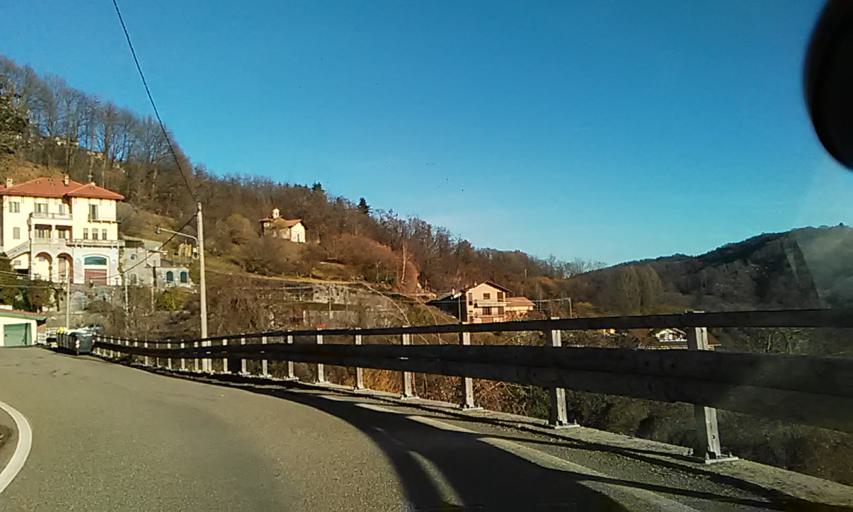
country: IT
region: Piedmont
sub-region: Provincia di Vercelli
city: Valduggia
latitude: 45.7431
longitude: 8.3456
